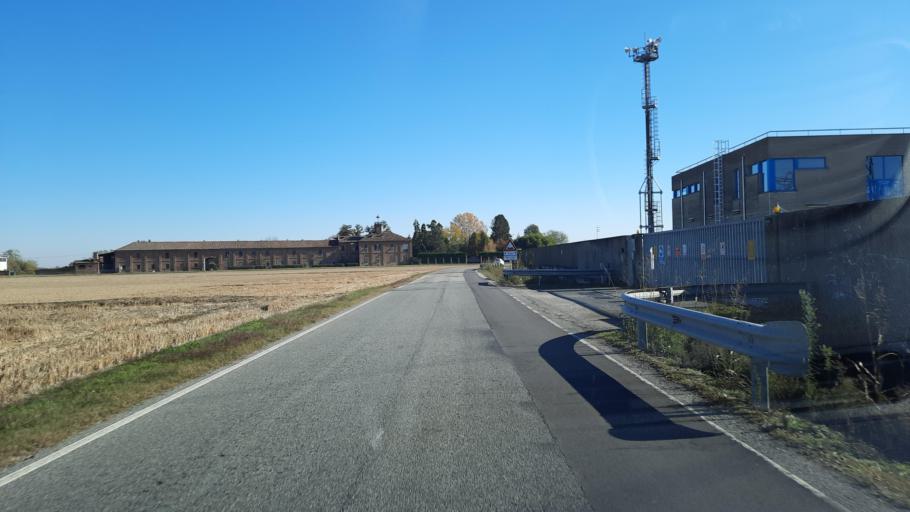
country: IT
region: Piedmont
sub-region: Provincia di Alessandria
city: Balzola
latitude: 45.1861
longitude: 8.4297
